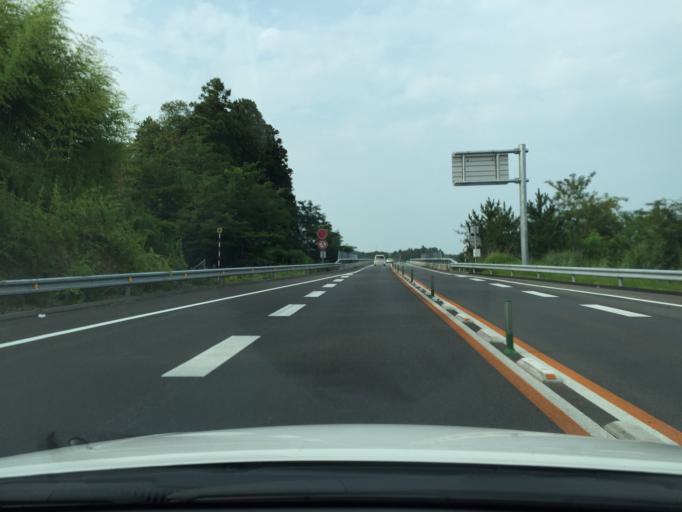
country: JP
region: Fukushima
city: Namie
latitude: 37.2895
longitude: 140.9823
